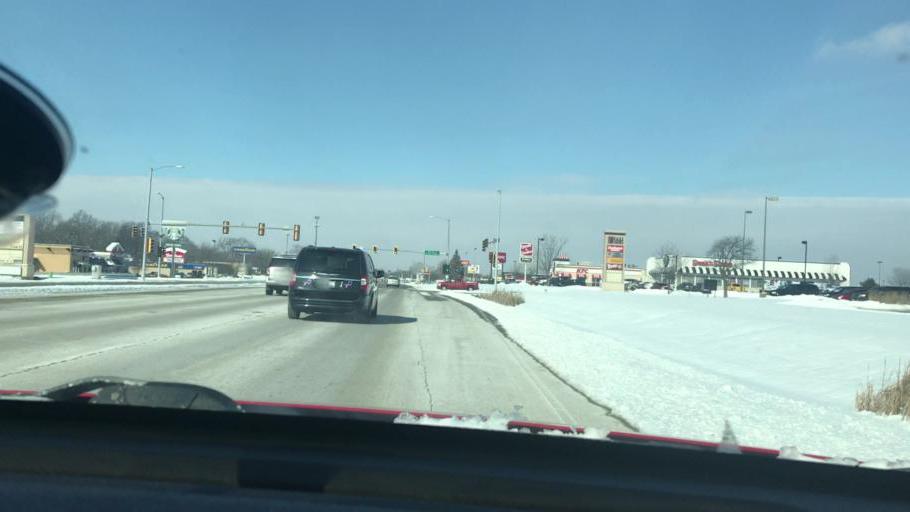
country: US
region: Illinois
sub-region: Tazewell County
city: Pekin
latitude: 40.5431
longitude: -89.5973
